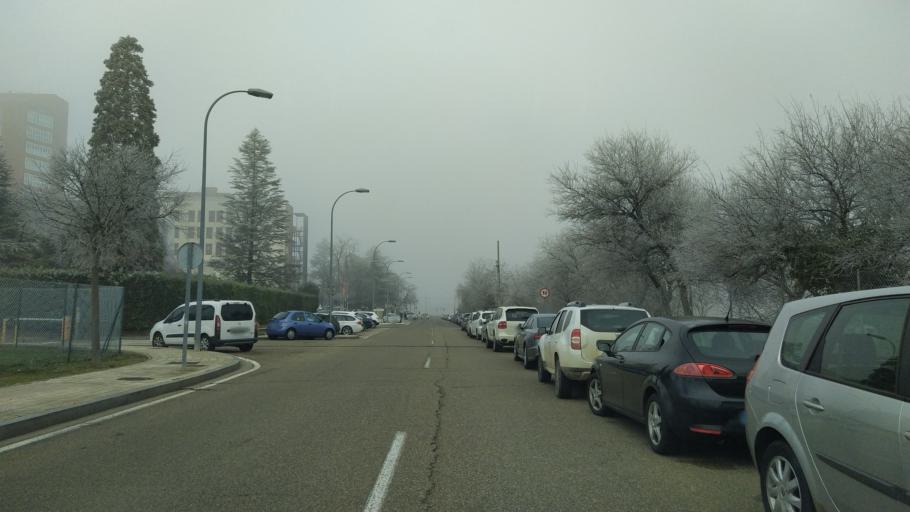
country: ES
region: Castille and Leon
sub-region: Provincia de Palencia
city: Palencia
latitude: 41.9997
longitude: -4.5382
